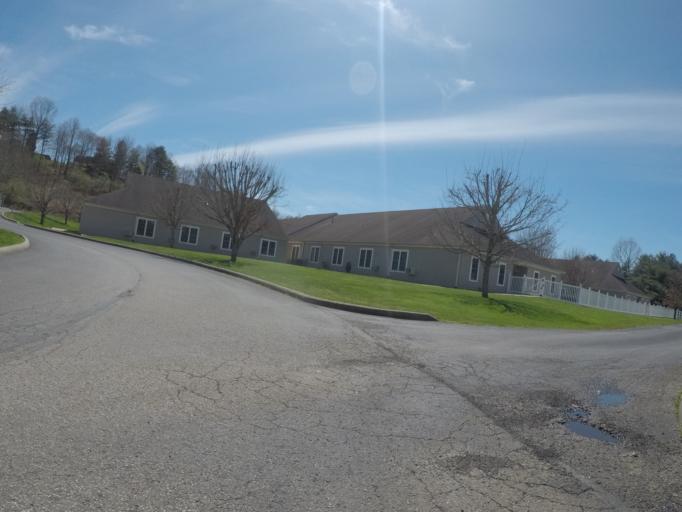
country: US
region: West Virginia
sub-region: Cabell County
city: Pea Ridge
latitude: 38.4076
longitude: -82.3133
